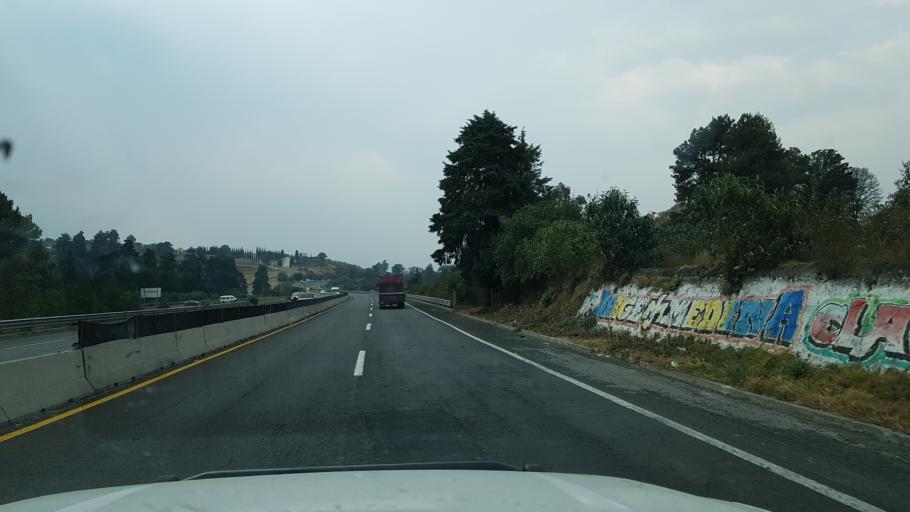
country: MX
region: Mexico
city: Tlalmanalco de Velazquez
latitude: 19.1881
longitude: -98.7989
